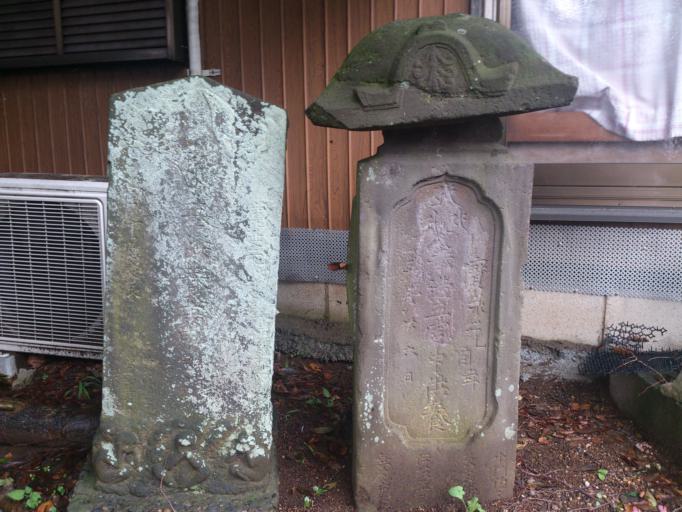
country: JP
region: Chiba
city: Matsudo
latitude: 35.7848
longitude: 139.9077
